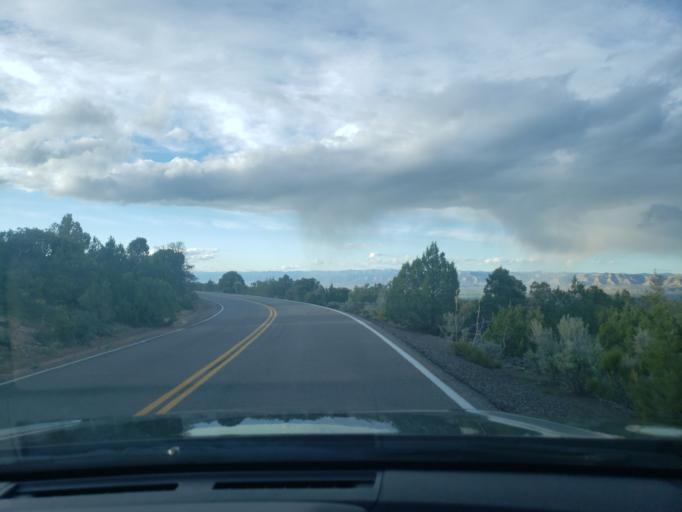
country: US
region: Colorado
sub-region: Mesa County
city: Redlands
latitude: 39.0312
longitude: -108.6600
